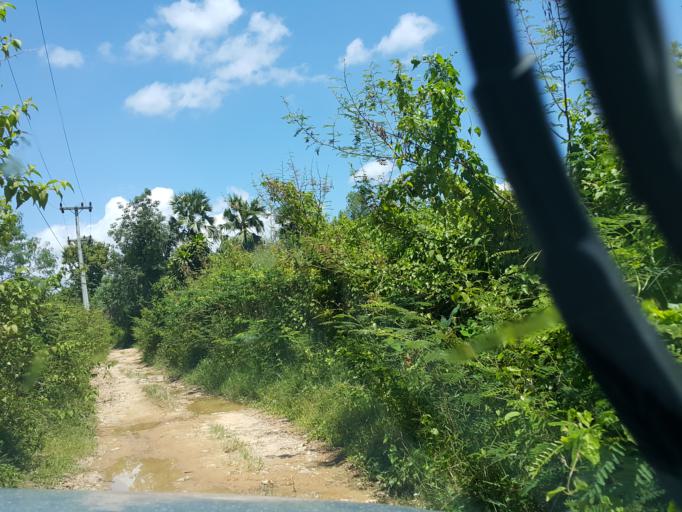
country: TH
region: Lamphun
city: Ban Thi
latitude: 18.6826
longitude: 99.1720
